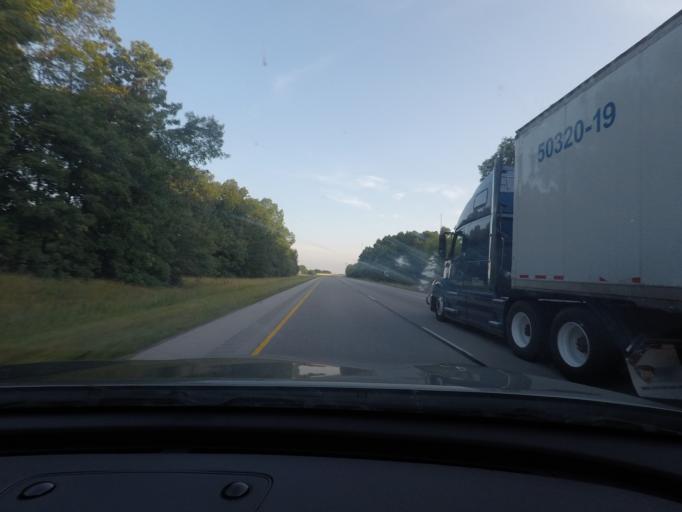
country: US
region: Illinois
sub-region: Johnson County
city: Goreville
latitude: 37.5507
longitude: -88.9378
